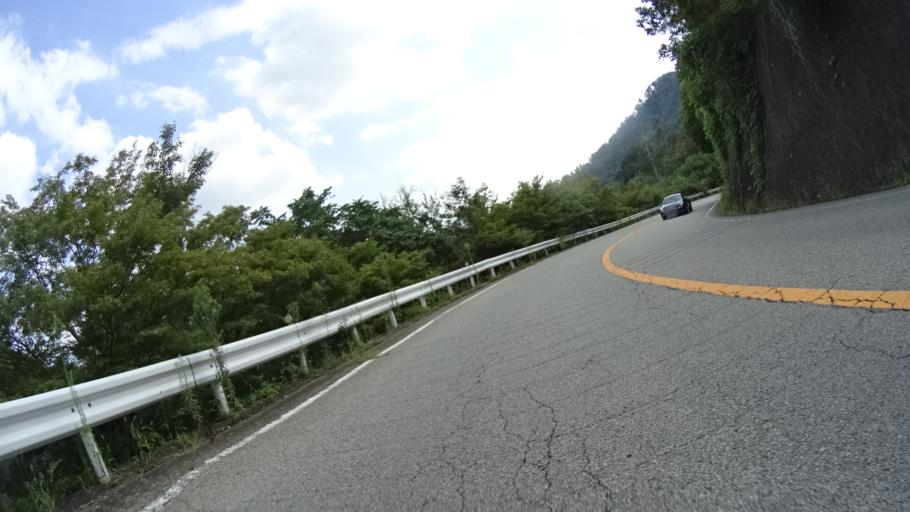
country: JP
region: Yamanashi
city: Kofu-shi
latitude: 35.6952
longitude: 138.5610
